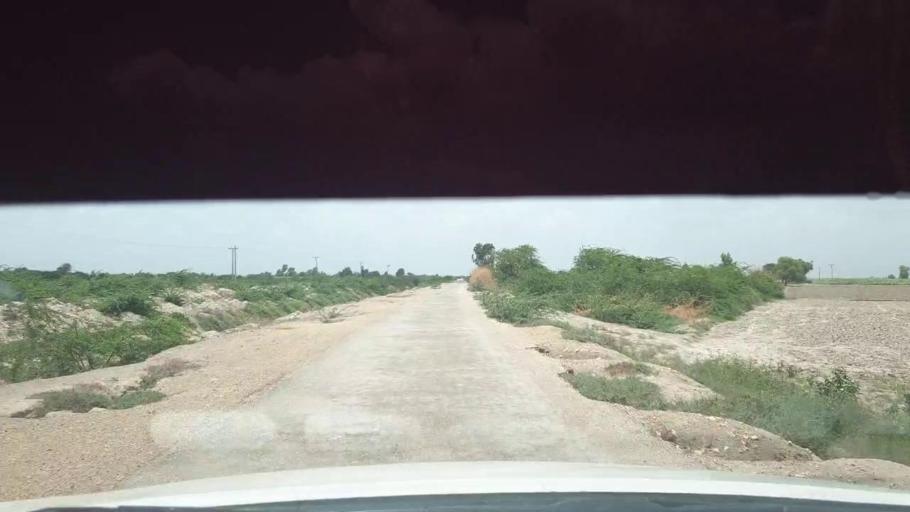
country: PK
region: Sindh
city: Kadhan
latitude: 24.5349
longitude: 69.1263
